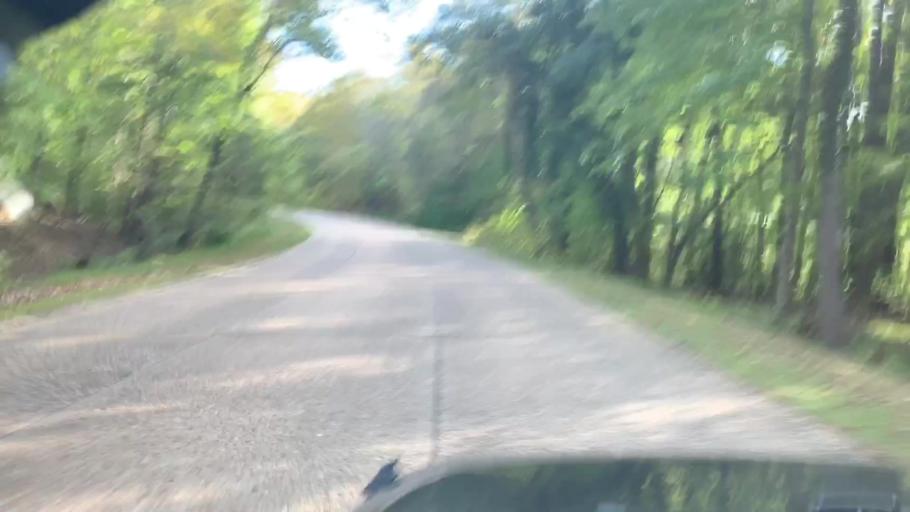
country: US
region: Virginia
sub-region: City of Williamsburg
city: Williamsburg
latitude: 37.2549
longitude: -76.7037
